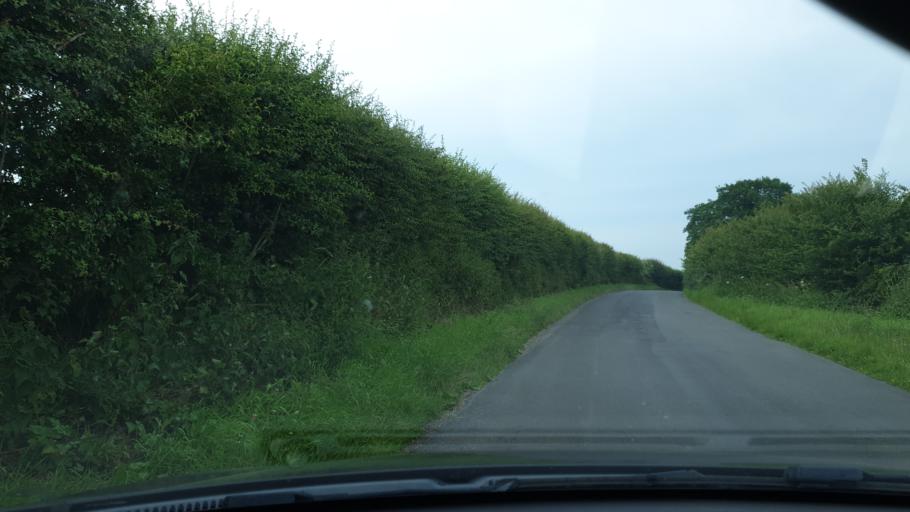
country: GB
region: England
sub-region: Suffolk
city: Shotley Gate
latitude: 51.9166
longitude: 1.2037
